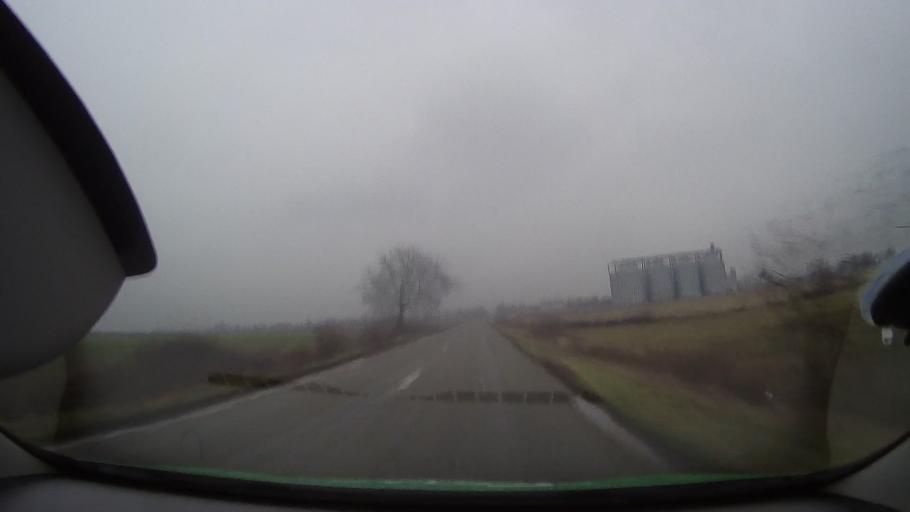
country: RO
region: Bihor
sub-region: Comuna Tulca
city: Tulca
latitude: 46.7948
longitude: 21.7370
